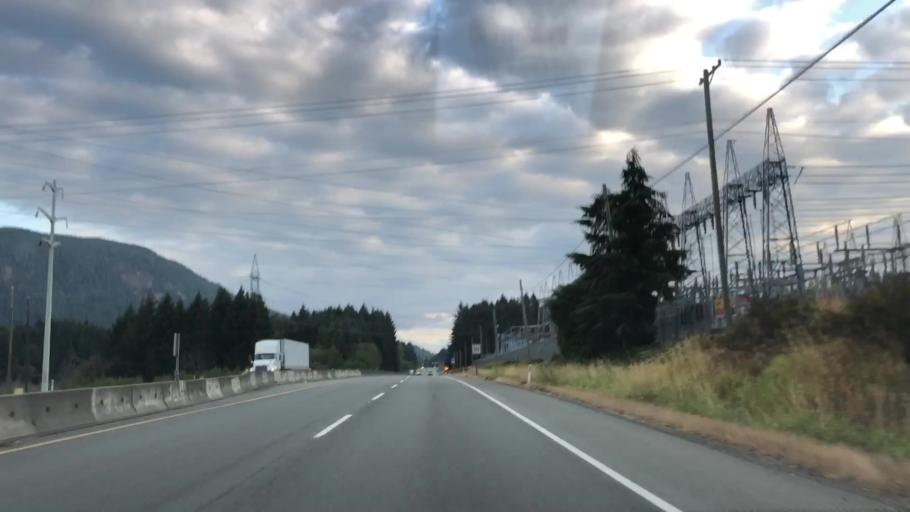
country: CA
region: British Columbia
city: North Cowichan
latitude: 48.8250
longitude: -123.7179
